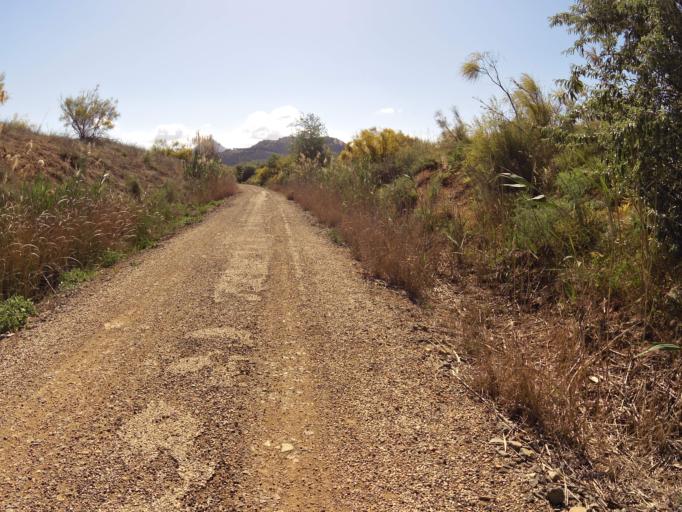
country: ES
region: Andalusia
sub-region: Provincia de Jaen
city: Alcaudete
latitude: 37.6032
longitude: -4.1494
